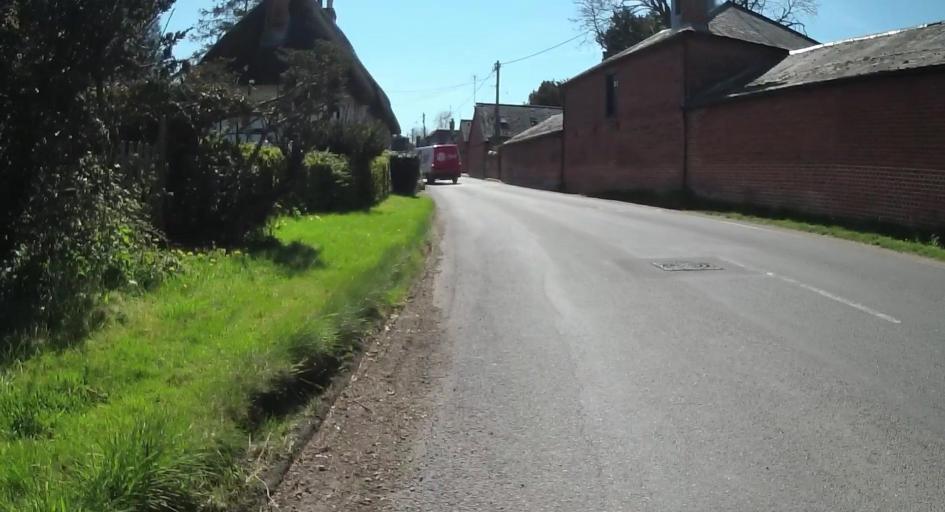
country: GB
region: England
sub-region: Hampshire
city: Romsey
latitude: 51.0777
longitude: -1.4847
